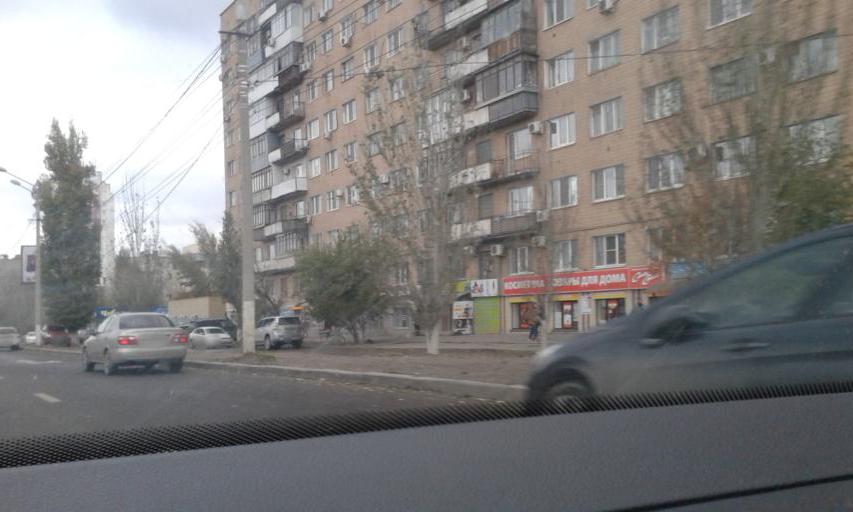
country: RU
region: Volgograd
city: Volgograd
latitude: 48.7233
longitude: 44.5130
